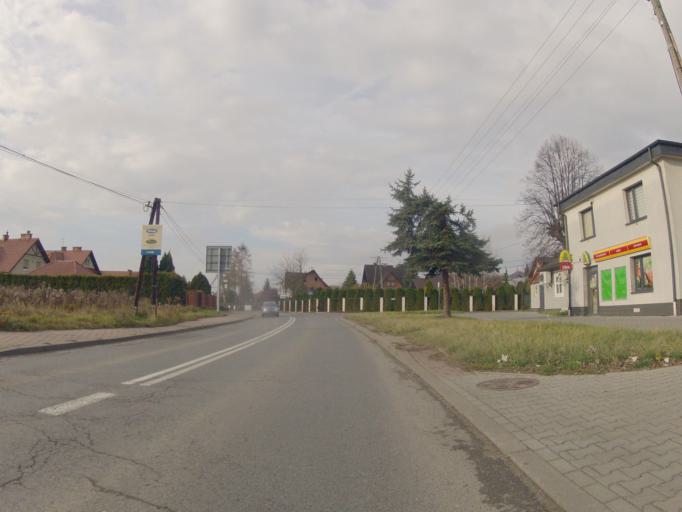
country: PL
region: Lesser Poland Voivodeship
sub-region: Powiat krakowski
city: Rzaska
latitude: 50.0914
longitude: 19.8331
